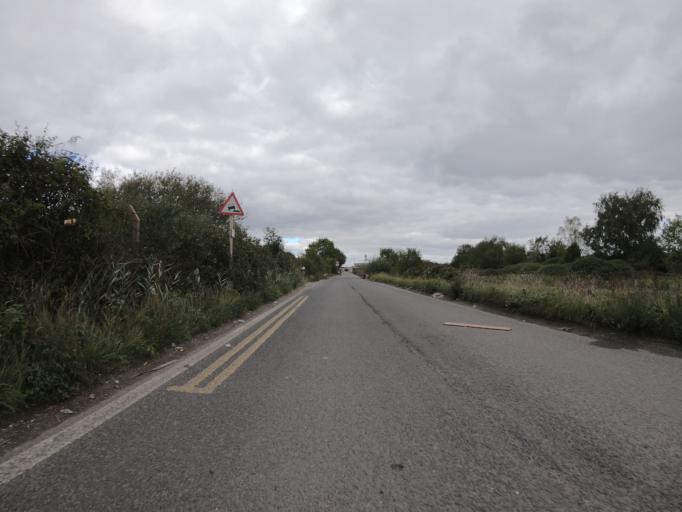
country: GB
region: England
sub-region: Essex
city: Purfleet
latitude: 51.4774
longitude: 0.2097
